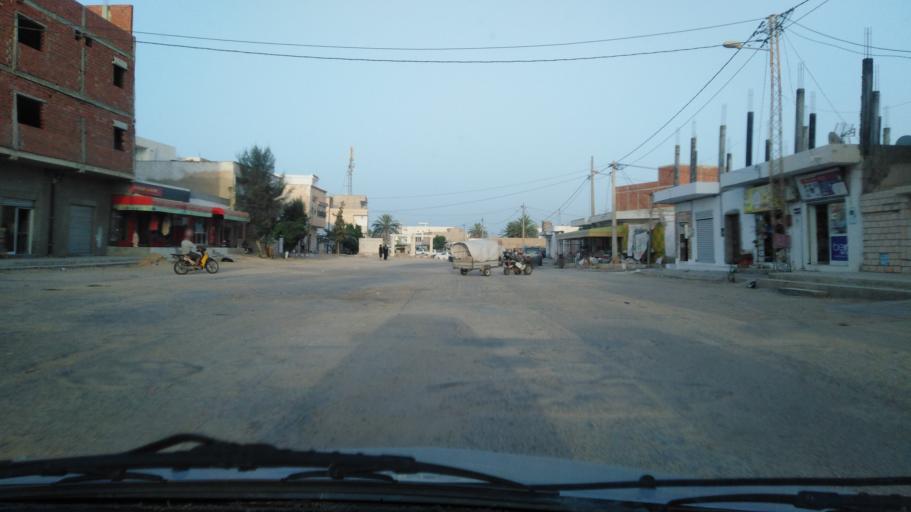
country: TN
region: Qabis
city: Gabes
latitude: 33.9594
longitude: 9.9989
